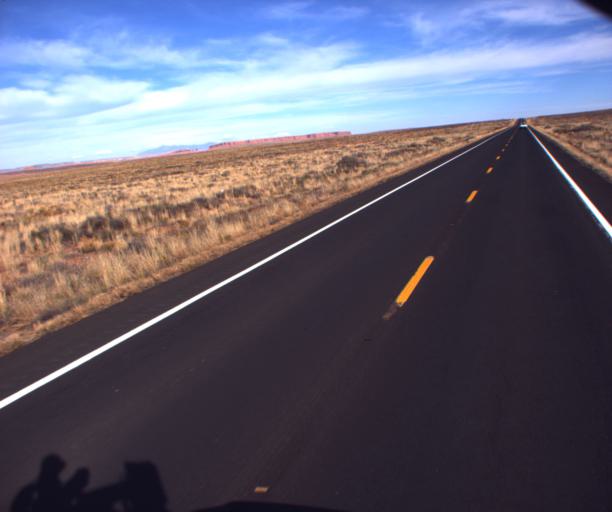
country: US
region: Arizona
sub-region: Apache County
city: Lukachukai
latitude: 36.9637
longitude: -109.4688
